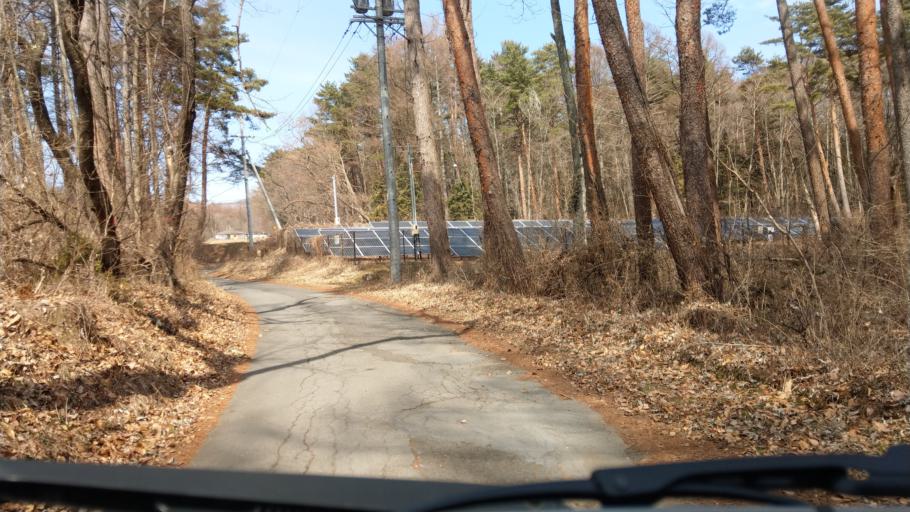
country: JP
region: Nagano
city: Komoro
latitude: 36.3381
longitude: 138.4635
